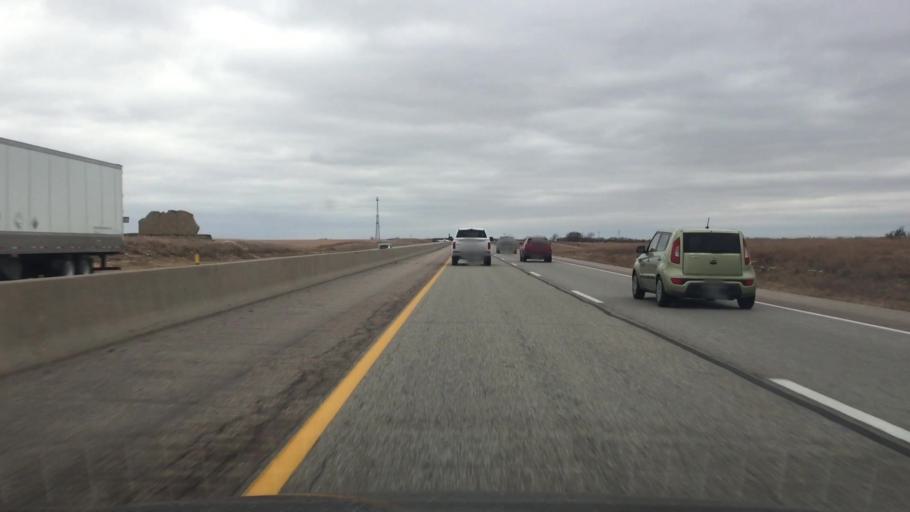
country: US
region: Kansas
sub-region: Butler County
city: El Dorado
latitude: 37.9682
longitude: -96.7244
